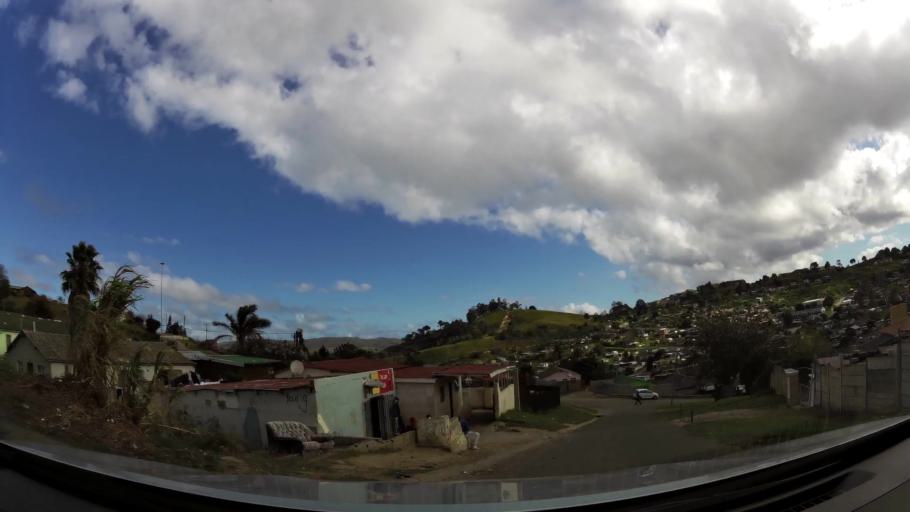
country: ZA
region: Western Cape
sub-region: Eden District Municipality
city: Knysna
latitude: -34.0518
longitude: 23.0959
